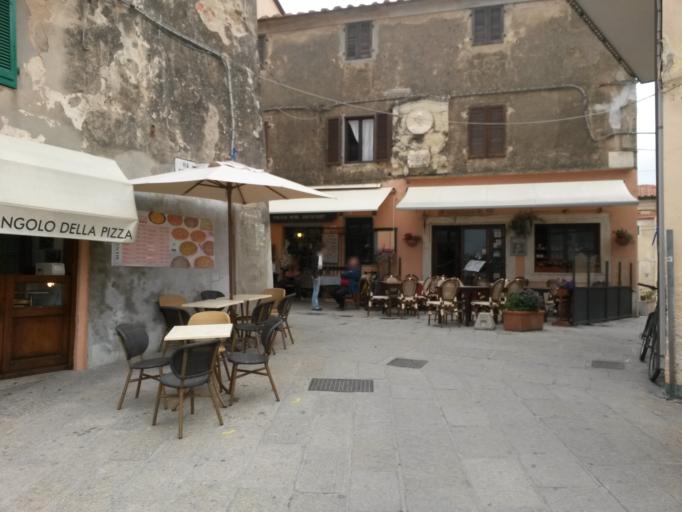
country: IT
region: Tuscany
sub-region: Provincia di Livorno
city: Capoliveri
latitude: 42.7455
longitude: 10.3776
